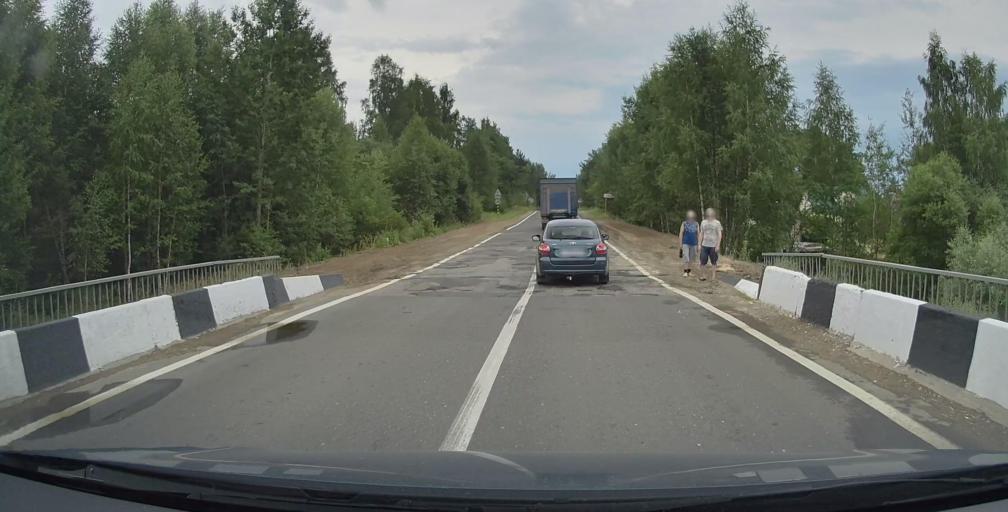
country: RU
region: Jaroslavl
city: Myshkin
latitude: 57.8552
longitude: 38.5099
